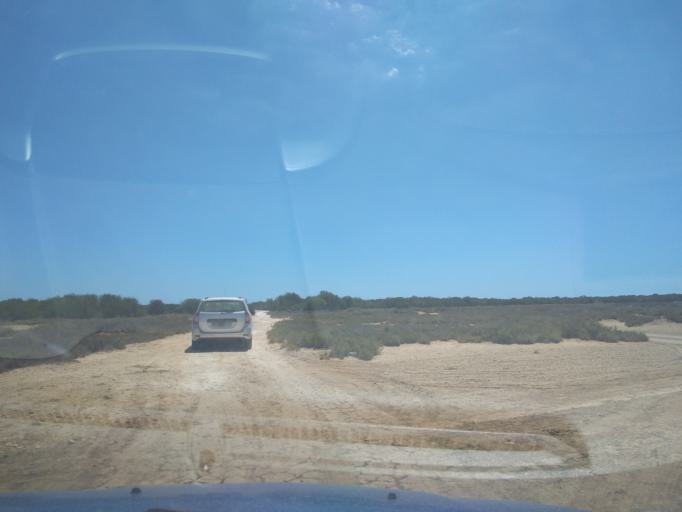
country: TN
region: Susah
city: Harqalah
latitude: 36.1627
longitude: 10.4602
